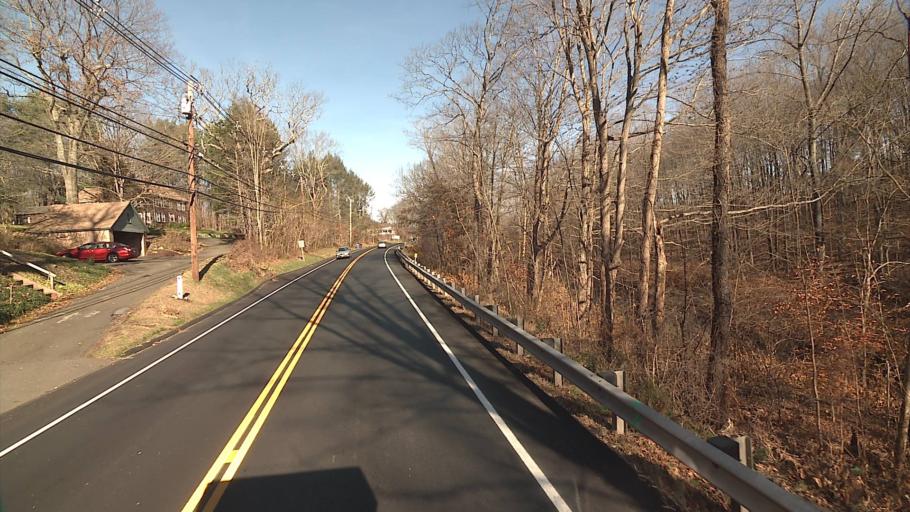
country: US
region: Connecticut
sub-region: New Haven County
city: Wallingford Center
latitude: 41.3982
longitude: -72.7866
